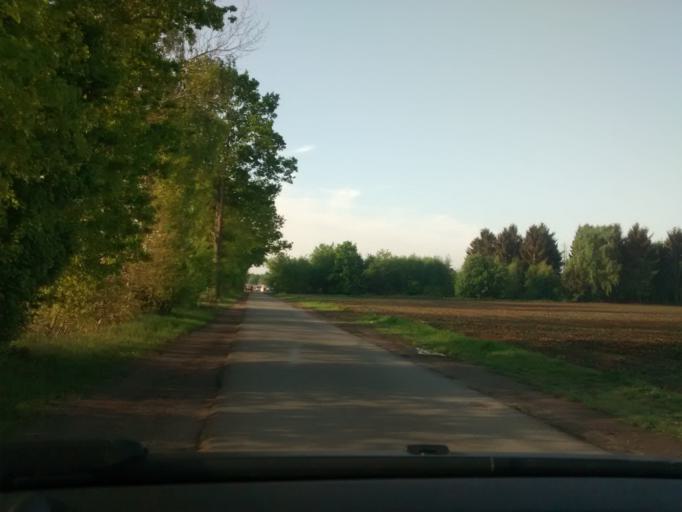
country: DE
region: Lower Saxony
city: Winsen
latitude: 53.3699
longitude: 10.1858
